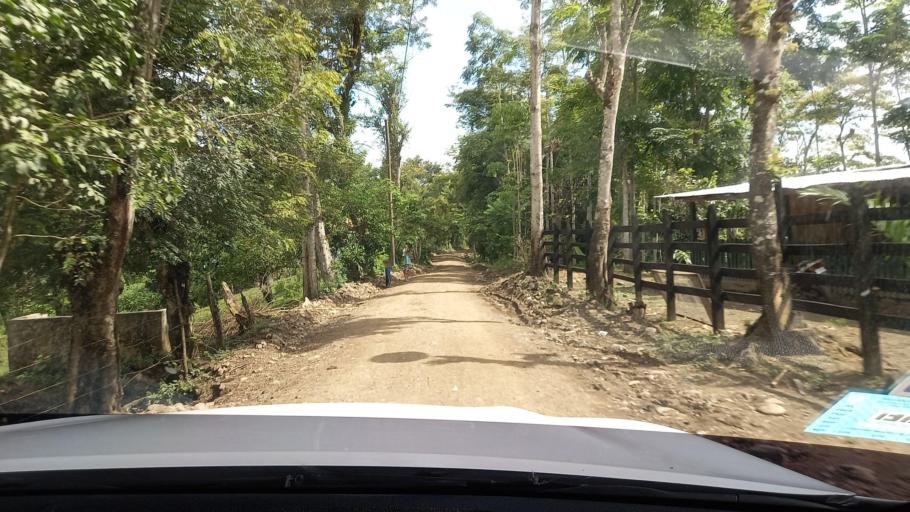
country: NI
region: Jinotega
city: San Jose de Bocay
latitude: 13.3799
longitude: -85.6850
